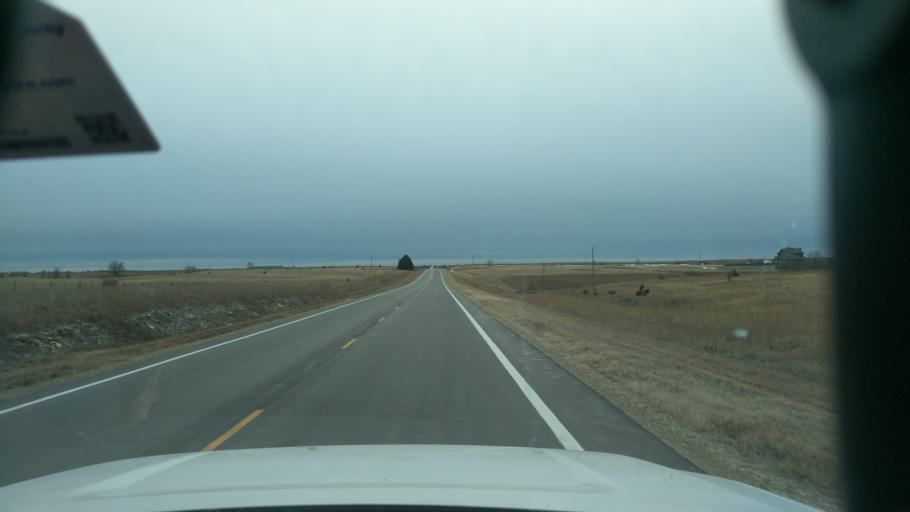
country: US
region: Kansas
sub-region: Dickinson County
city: Herington
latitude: 38.7323
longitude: -96.9275
